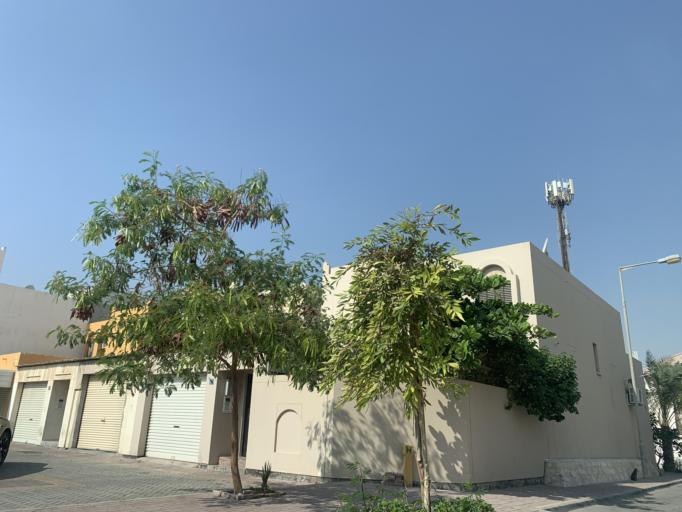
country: BH
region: Central Governorate
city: Madinat Hamad
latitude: 26.1246
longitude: 50.4912
